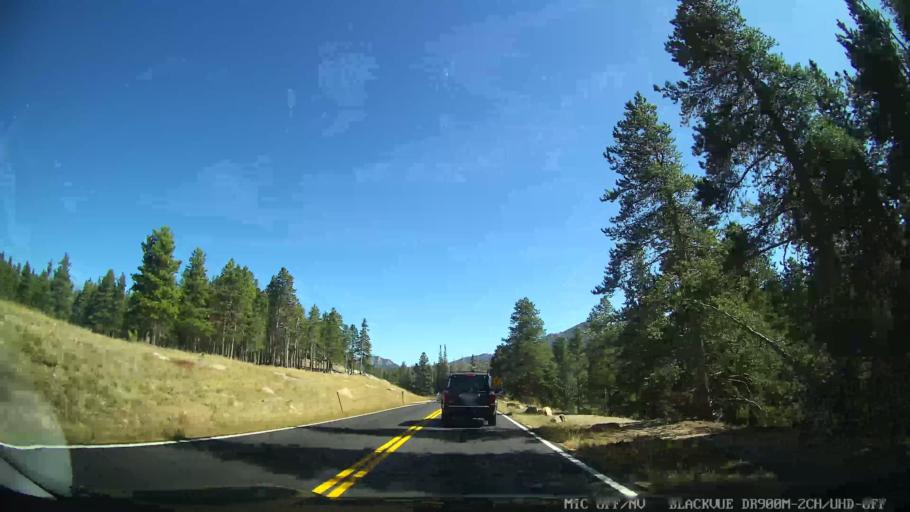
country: US
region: Colorado
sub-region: Larimer County
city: Estes Park
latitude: 40.3250
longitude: -105.6062
